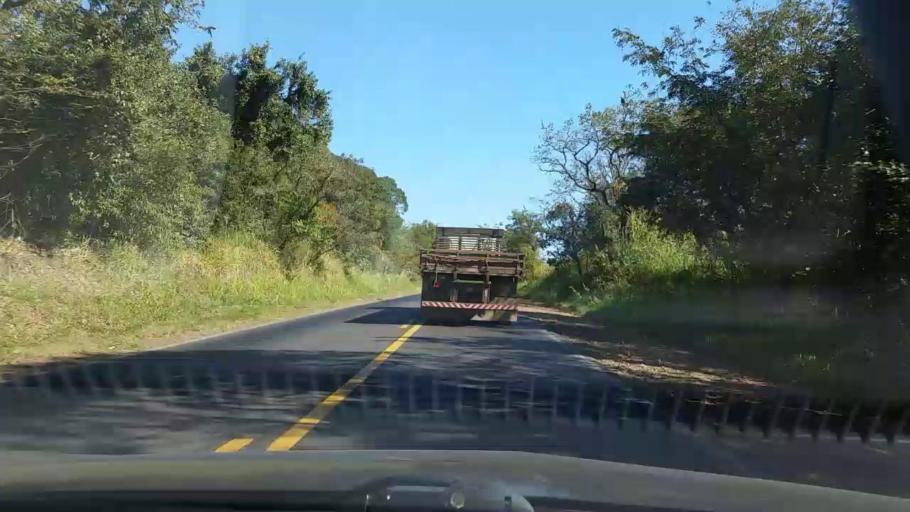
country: BR
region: Sao Paulo
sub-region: Sao Manuel
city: Sao Manuel
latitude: -22.8122
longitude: -48.6780
